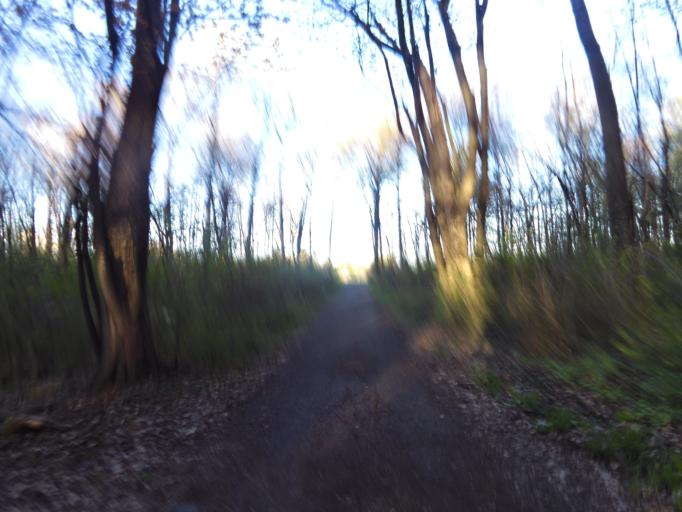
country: CA
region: Ontario
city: Bells Corners
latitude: 45.3389
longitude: -75.7562
